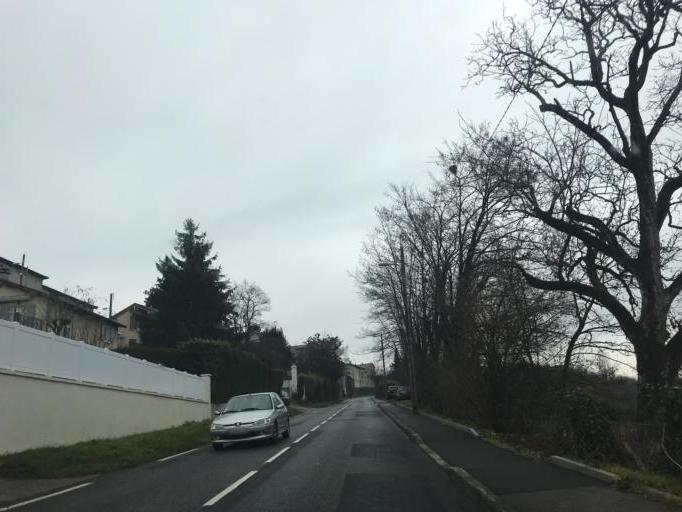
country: FR
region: Rhone-Alpes
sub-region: Departement du Rhone
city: Fontaines-Saint-Martin
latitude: 45.8464
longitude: 4.8568
